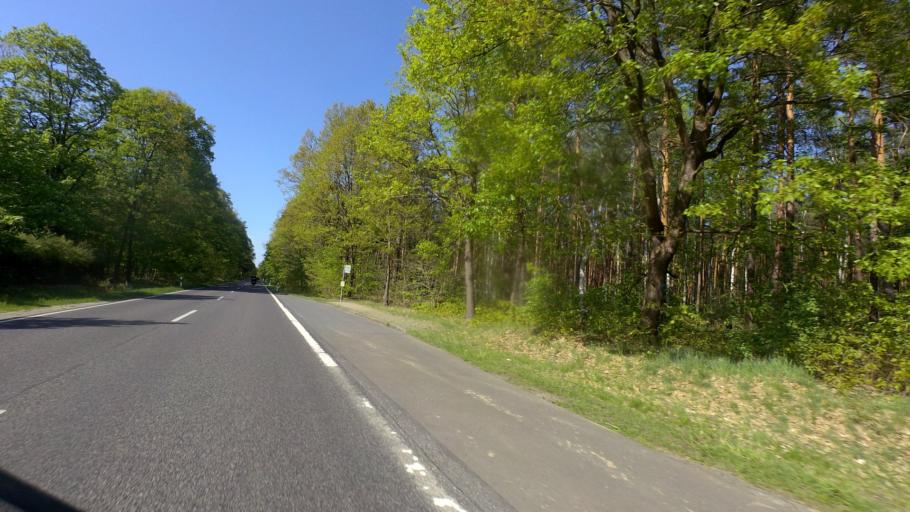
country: DE
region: Brandenburg
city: Gross Koris
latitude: 52.2124
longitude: 13.6886
